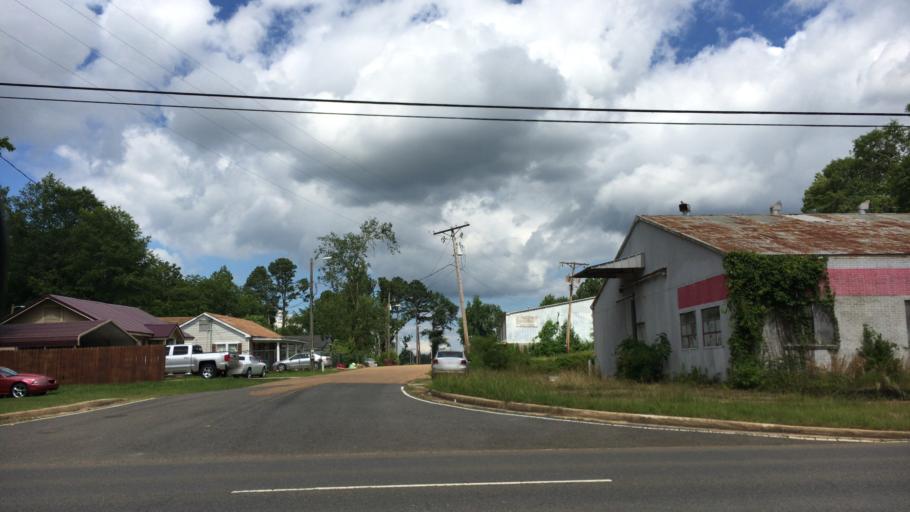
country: US
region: Louisiana
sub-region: Lincoln Parish
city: Ruston
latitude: 32.5094
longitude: -92.6375
